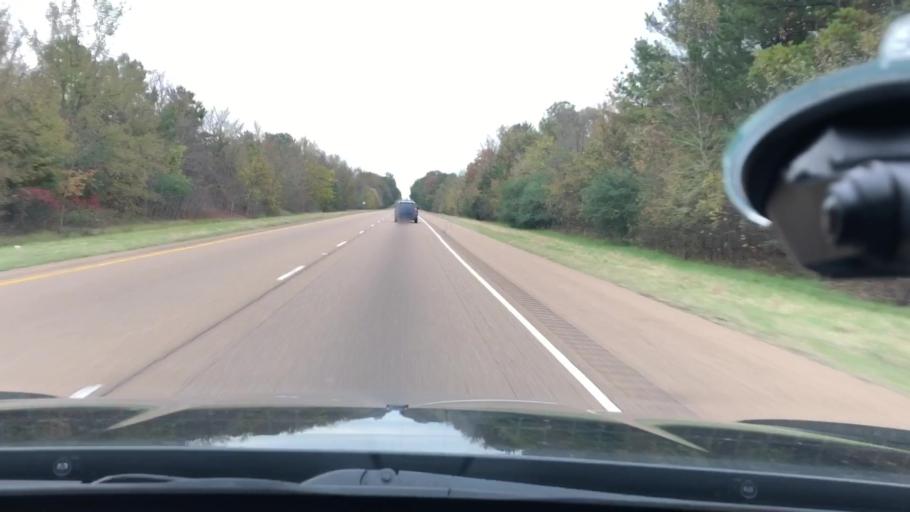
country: US
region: Arkansas
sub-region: Nevada County
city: Prescott
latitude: 33.7822
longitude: -93.4618
